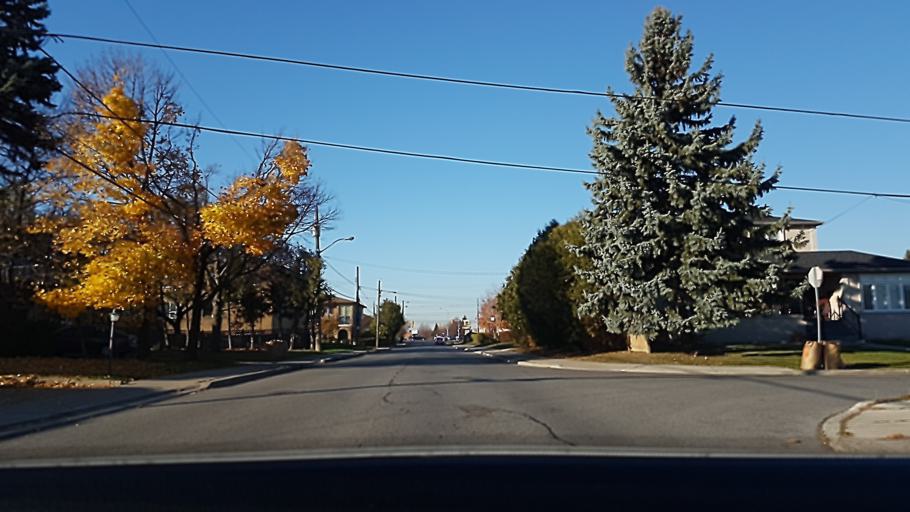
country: CA
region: Ontario
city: Concord
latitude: 43.7617
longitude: -79.4623
